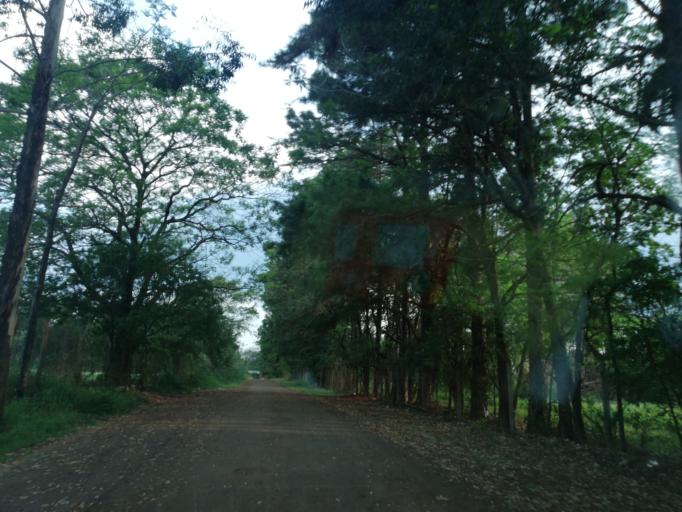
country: AR
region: Misiones
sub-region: Departamento de Capital
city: Posadas
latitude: -27.3978
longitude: -55.9733
